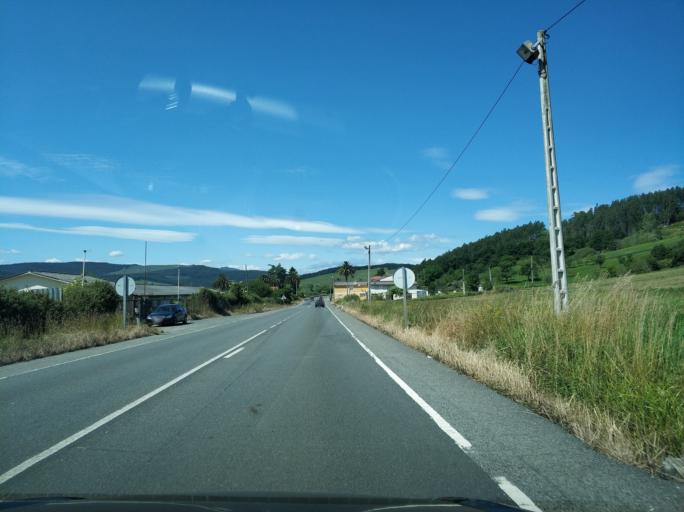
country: ES
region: Cantabria
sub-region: Provincia de Cantabria
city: Camargo
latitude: 43.3656
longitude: -3.9099
